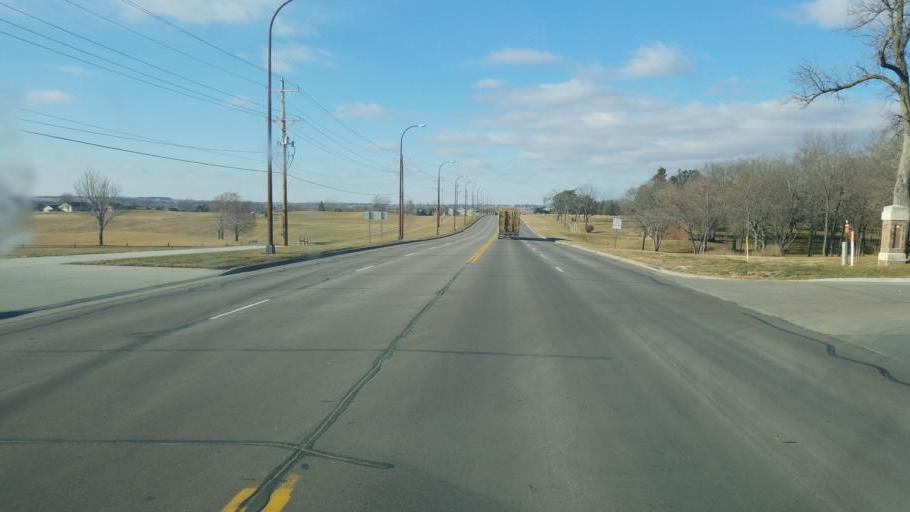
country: US
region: South Dakota
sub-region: Yankton County
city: Yankton
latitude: 42.9088
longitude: -97.4039
